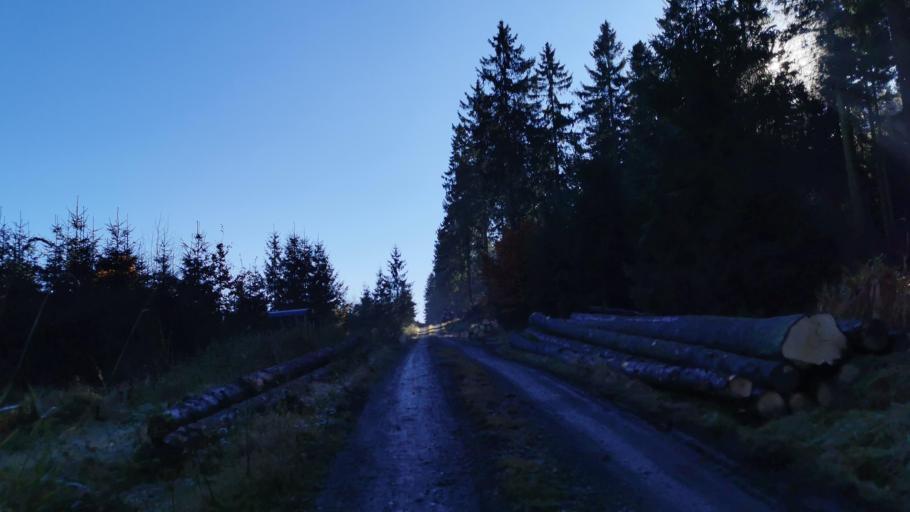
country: DE
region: Thuringia
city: Wurzbach
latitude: 50.4281
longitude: 11.5132
